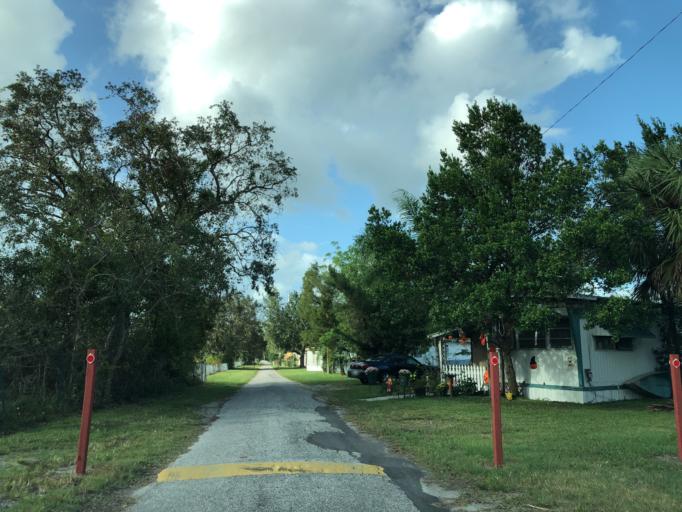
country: US
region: Florida
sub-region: Orange County
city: Bithlo
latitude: 28.5619
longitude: -81.1561
